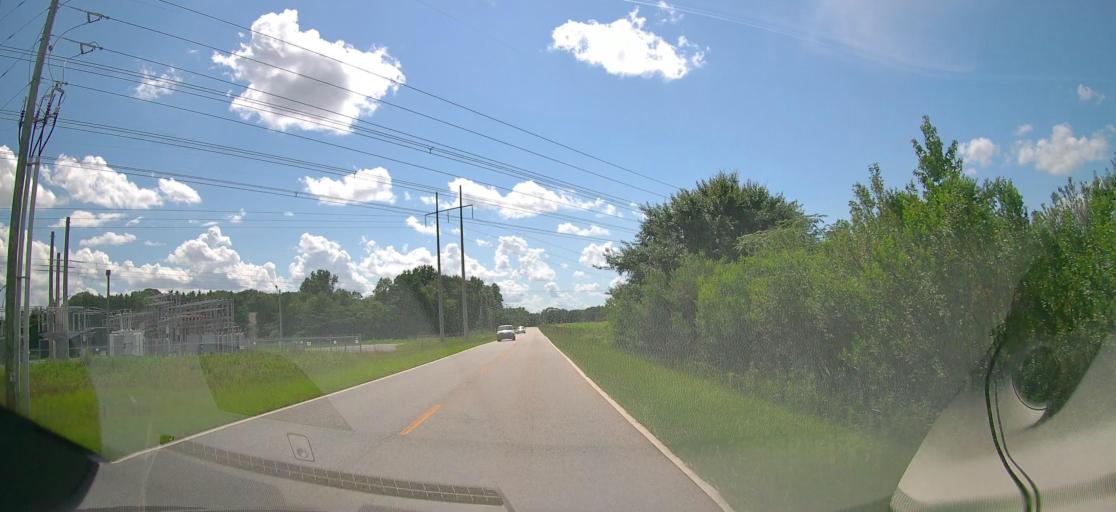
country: US
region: Georgia
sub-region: Houston County
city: Centerville
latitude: 32.6186
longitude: -83.7269
